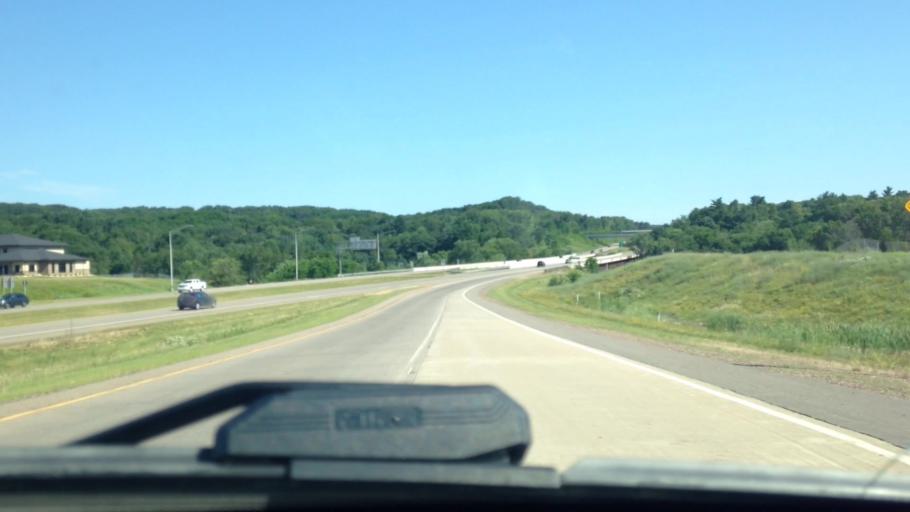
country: US
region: Wisconsin
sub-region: Eau Claire County
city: Altoona
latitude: 44.8195
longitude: -91.4536
